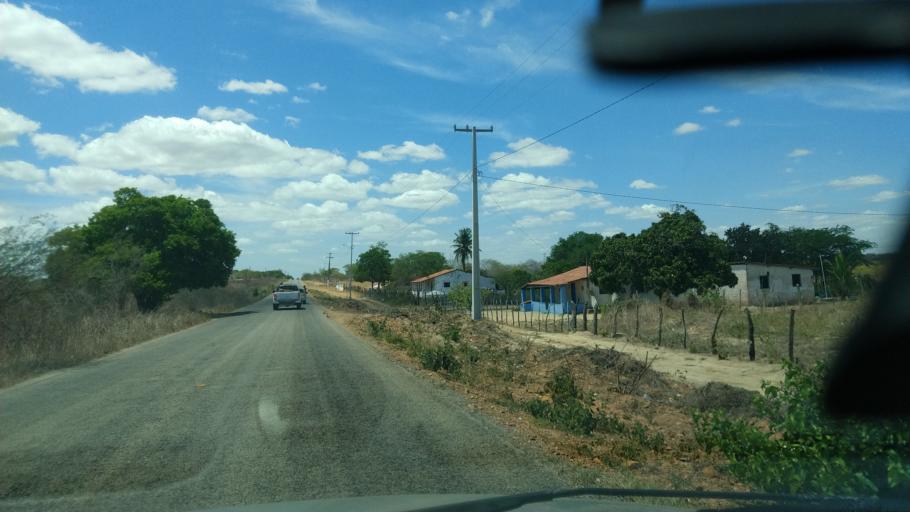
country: BR
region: Rio Grande do Norte
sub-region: Sao Paulo Do Potengi
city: Sao Paulo do Potengi
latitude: -5.9154
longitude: -35.7322
